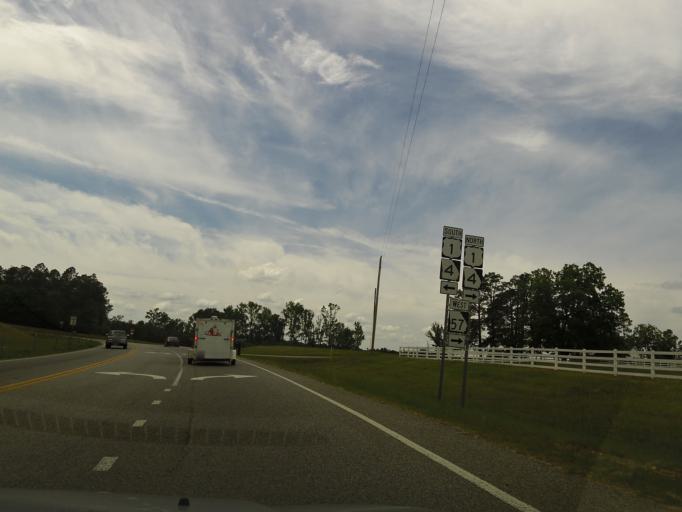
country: US
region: Georgia
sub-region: Emanuel County
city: Swainsboro
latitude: 32.5248
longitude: -82.2993
